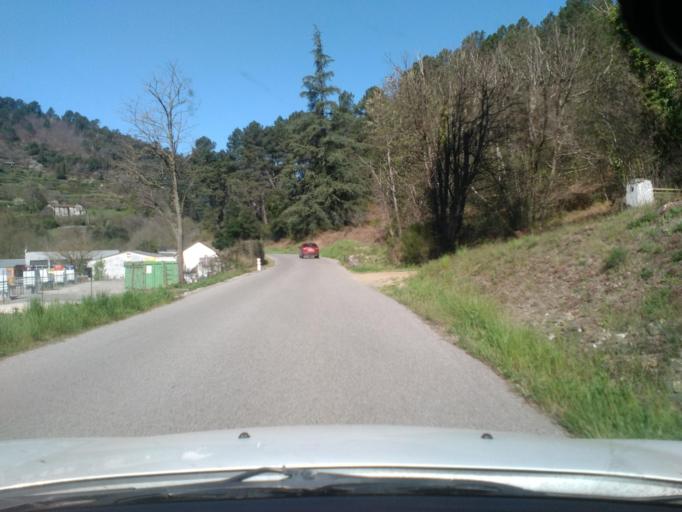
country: FR
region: Languedoc-Roussillon
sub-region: Departement du Gard
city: Valleraugue
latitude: 44.1753
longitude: 3.7547
